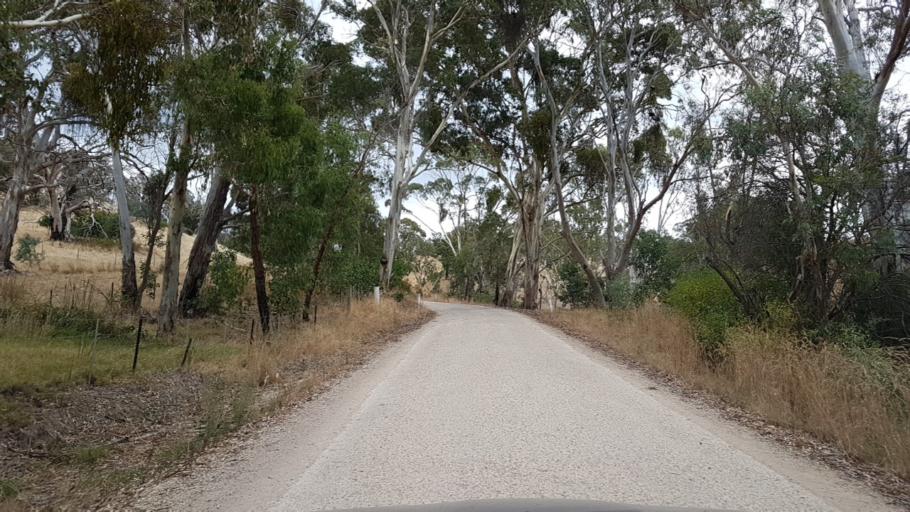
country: AU
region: South Australia
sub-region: Adelaide Hills
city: Gumeracha
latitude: -34.8011
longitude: 138.8228
